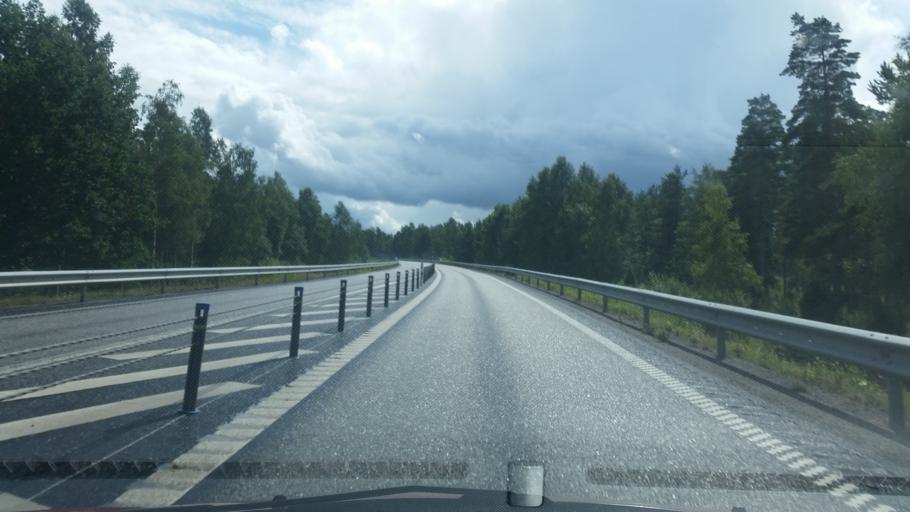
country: SE
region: Joenkoeping
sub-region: Gislaveds Kommun
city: Gislaved
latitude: 57.2741
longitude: 13.6171
